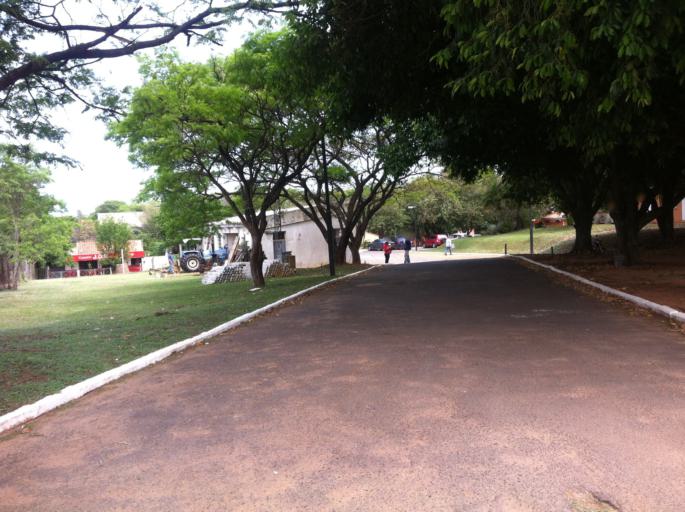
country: PY
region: Central
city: San Lorenzo
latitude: -25.2958
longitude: -57.4908
